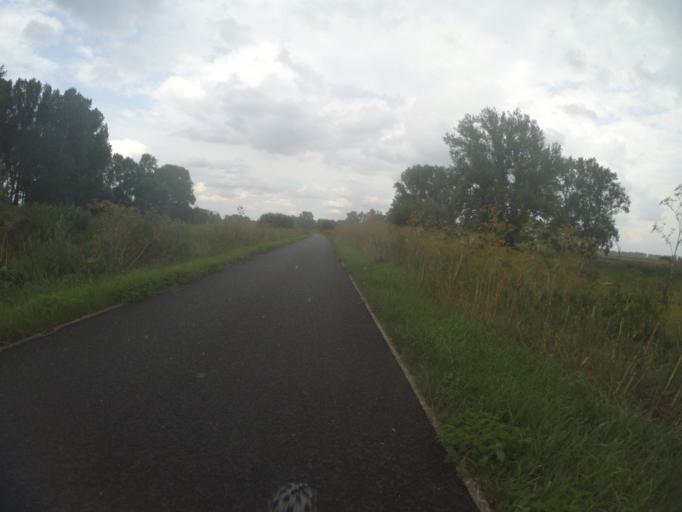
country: CZ
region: Central Bohemia
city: Luzec nad Vltavou
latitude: 50.3190
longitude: 14.4426
